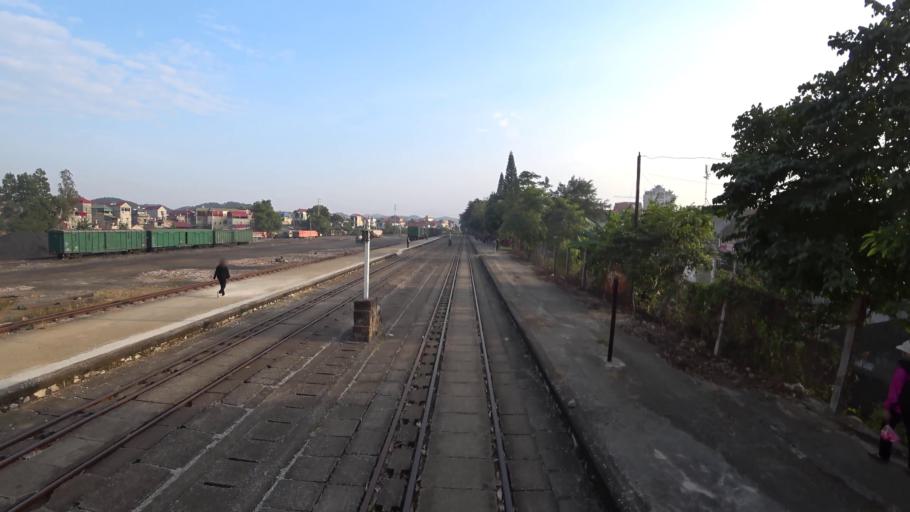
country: VN
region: Lang Son
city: Thi Tran Cao Loc
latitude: 21.8661
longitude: 106.7636
